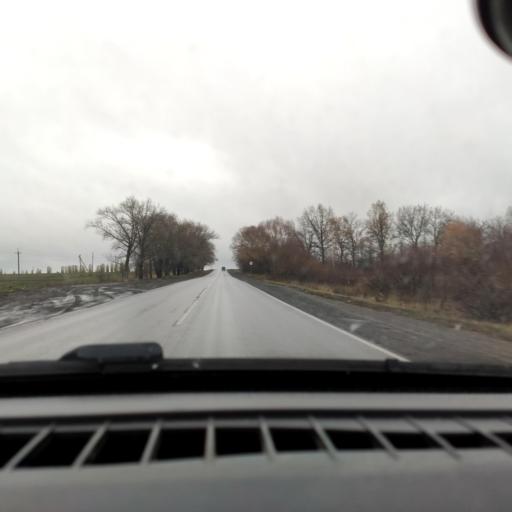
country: RU
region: Belgorod
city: Ilovka
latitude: 50.6933
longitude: 38.6593
